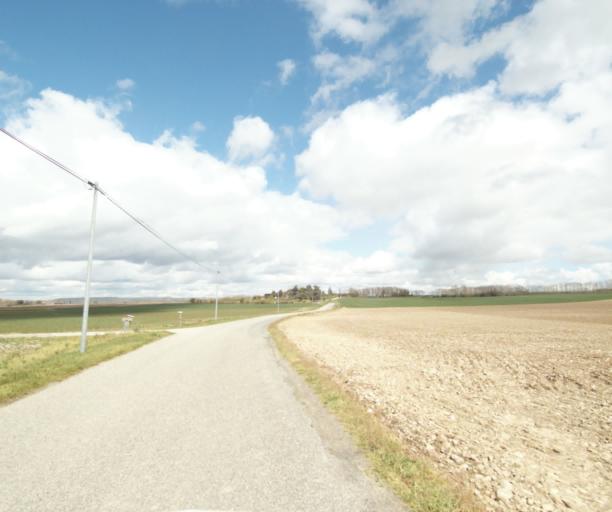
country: FR
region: Midi-Pyrenees
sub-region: Departement de l'Ariege
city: Saverdun
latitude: 43.2422
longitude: 1.5866
